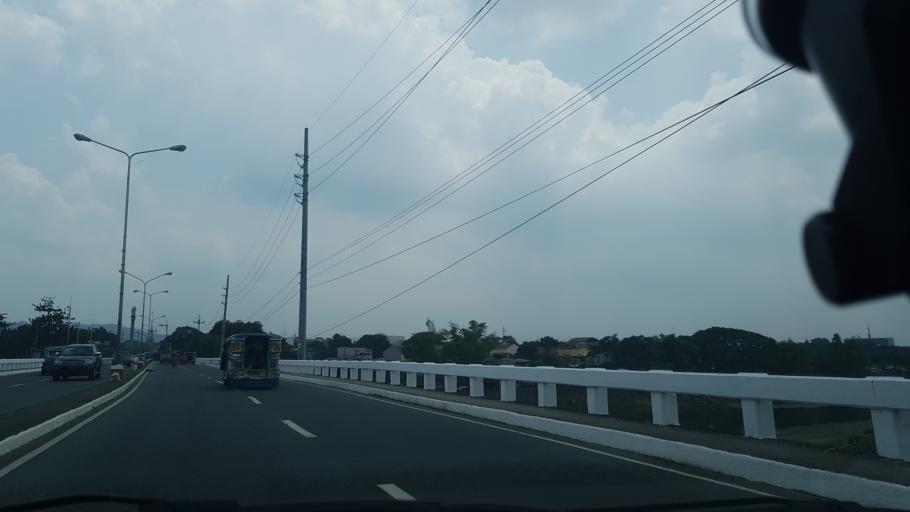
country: PH
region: Calabarzon
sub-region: Province of Rizal
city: San Mateo
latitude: 14.6802
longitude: 121.1089
